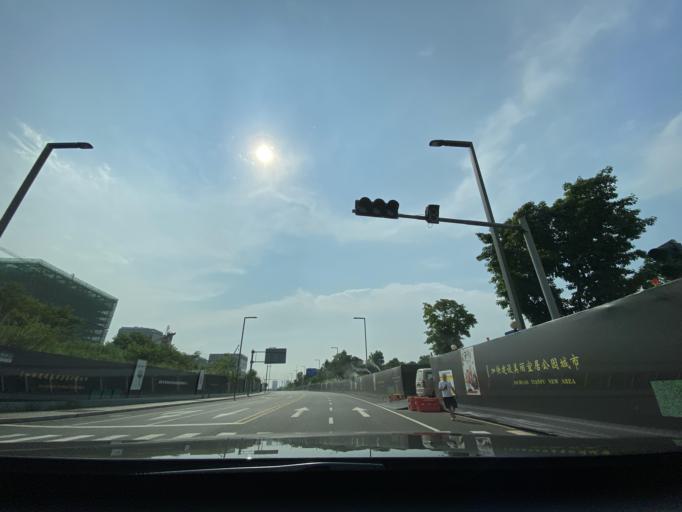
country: CN
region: Sichuan
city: Longquan
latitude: 30.3922
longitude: 104.0897
